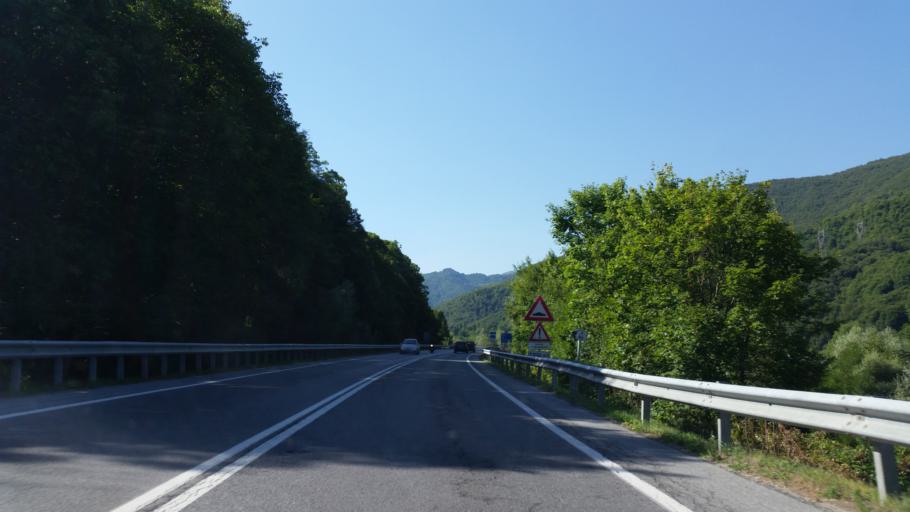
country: IT
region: Piedmont
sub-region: Provincia di Cuneo
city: Robilante
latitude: 44.2859
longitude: 7.5193
